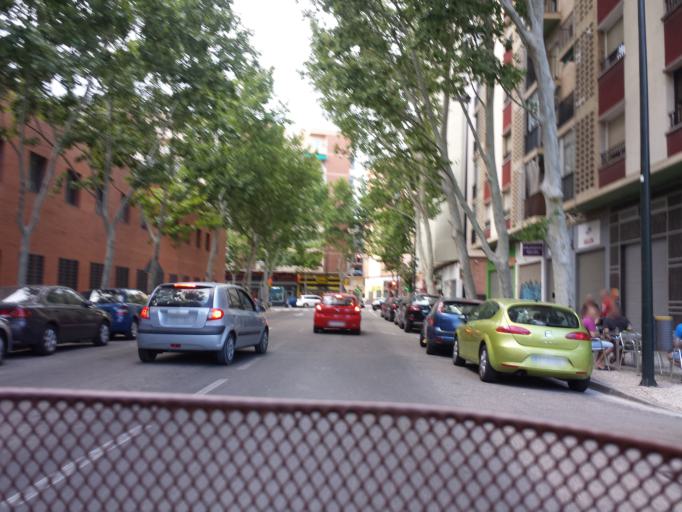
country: ES
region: Aragon
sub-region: Provincia de Zaragoza
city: Zaragoza
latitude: 41.6606
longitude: -0.8587
